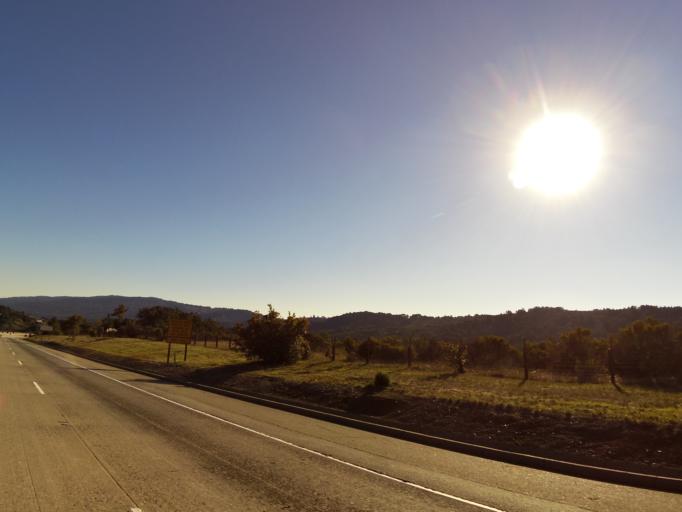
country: US
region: California
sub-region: San Mateo County
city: Highlands-Baywood Park
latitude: 37.5367
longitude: -122.3641
